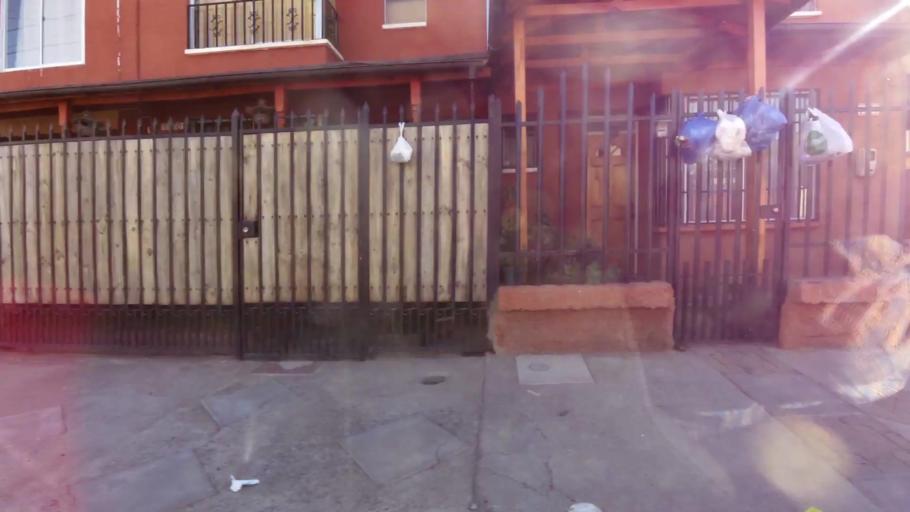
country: CL
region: O'Higgins
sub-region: Provincia de Cachapoal
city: Rancagua
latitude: -34.1868
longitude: -70.7616
